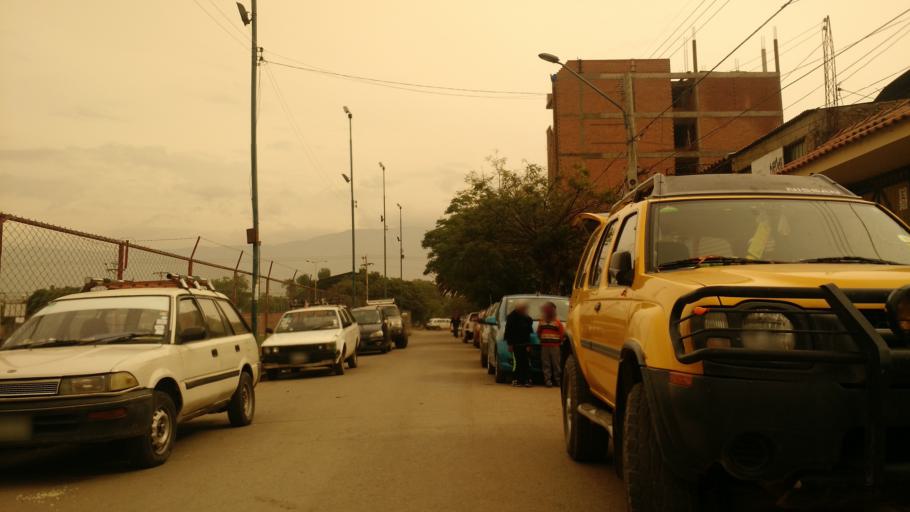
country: BO
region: Cochabamba
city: Cochabamba
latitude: -17.4266
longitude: -66.1558
